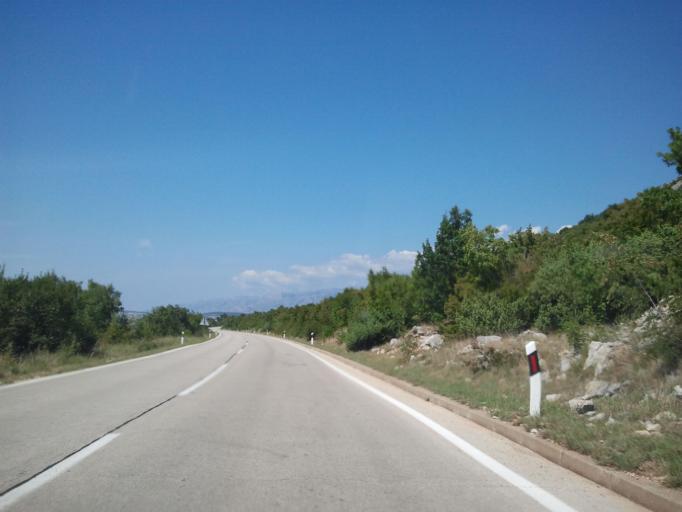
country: HR
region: Zadarska
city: Krusevo
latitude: 44.1711
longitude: 15.6229
